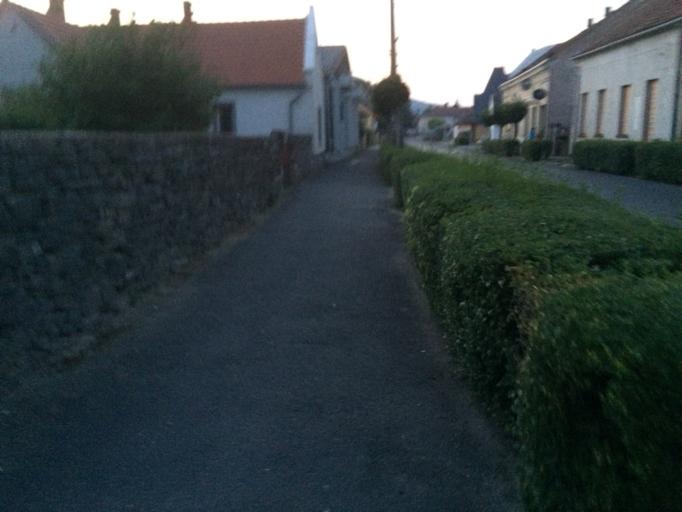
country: HU
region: Veszprem
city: Badacsonytomaj
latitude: 46.8044
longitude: 17.5145
